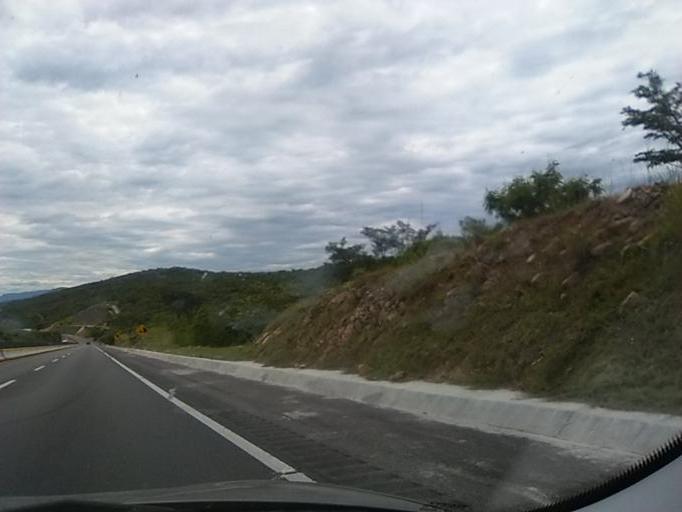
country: MX
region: Guerrero
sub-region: Huitzuco de los Figueroa
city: Ciudad de Huitzuco
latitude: 18.1525
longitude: -99.2127
